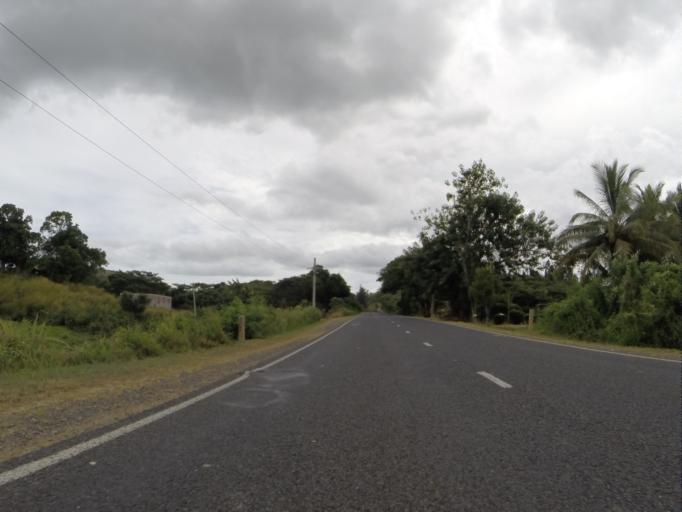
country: FJ
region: Western
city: Nadi
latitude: -18.0065
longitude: 177.3204
